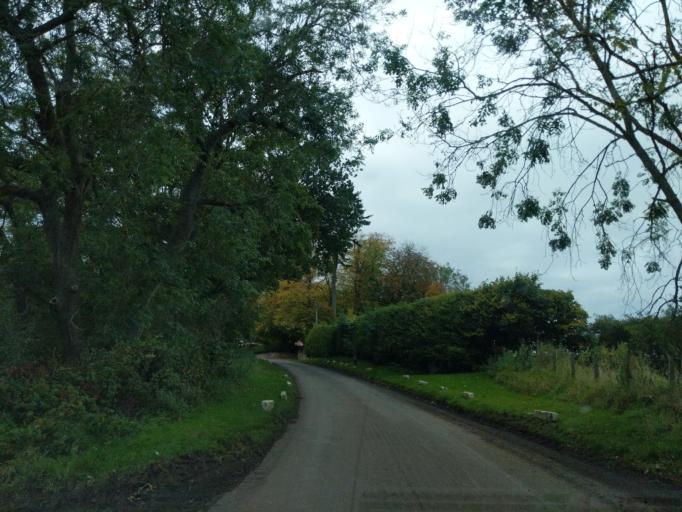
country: GB
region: Scotland
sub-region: East Lothian
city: Haddington
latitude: 55.9290
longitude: -2.8221
